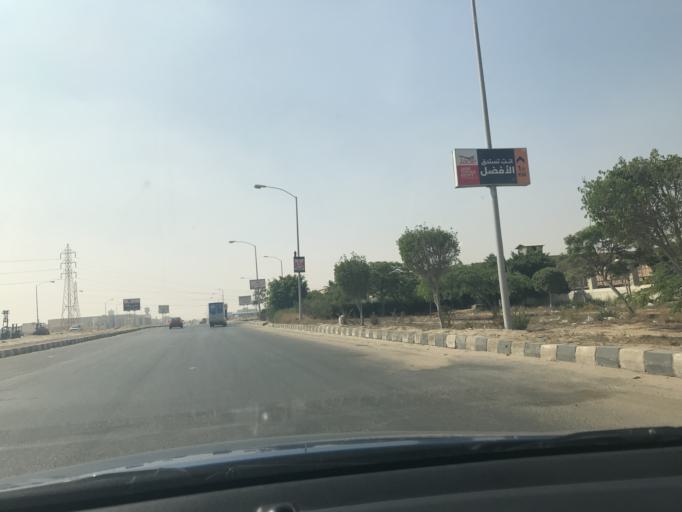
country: EG
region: Eastern Province
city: Bilbays
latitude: 30.2494
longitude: 31.7600
